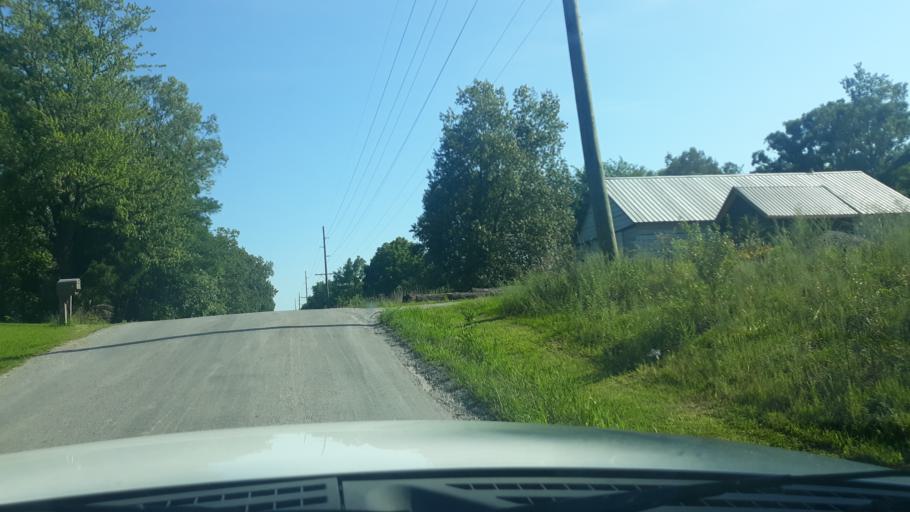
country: US
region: Illinois
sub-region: Saline County
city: Harrisburg
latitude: 37.8551
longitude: -88.5964
